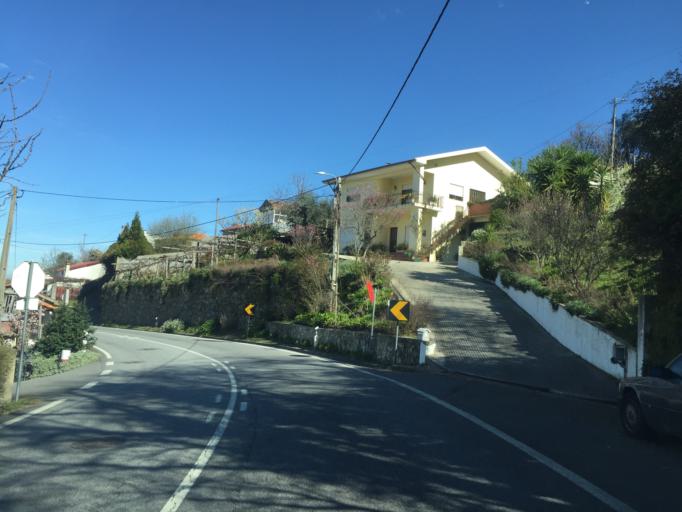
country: PT
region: Aveiro
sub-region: Vale de Cambra
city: Macieira de Cambra
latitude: 40.8946
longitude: -8.3305
